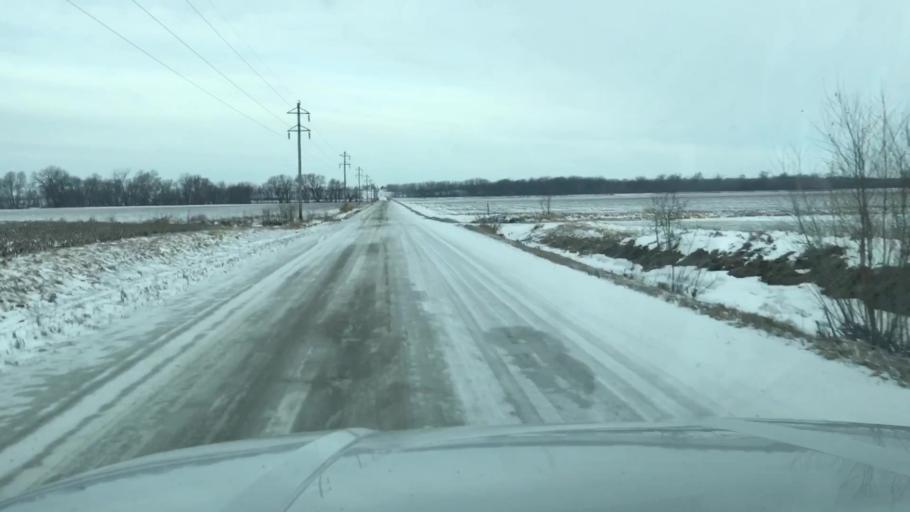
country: US
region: Missouri
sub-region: Holt County
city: Oregon
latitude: 40.1301
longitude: -95.0357
